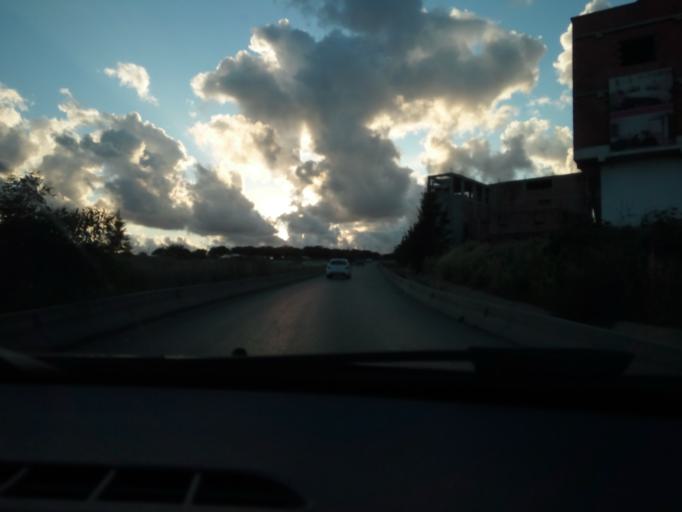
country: DZ
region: Tipaza
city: Saoula
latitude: 36.6521
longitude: 3.0143
